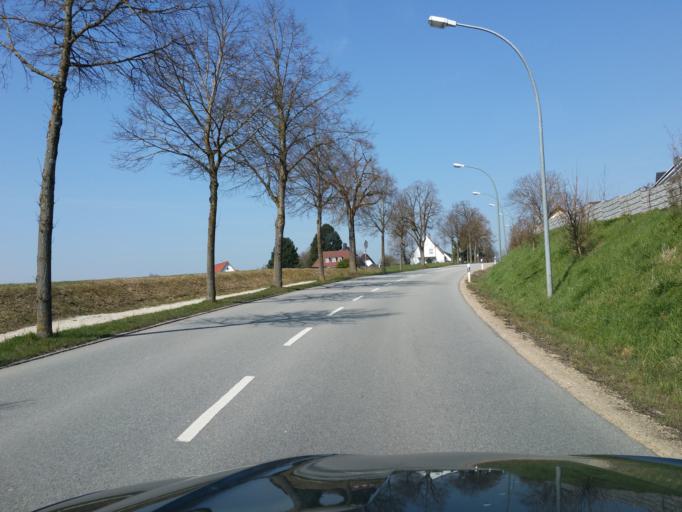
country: DE
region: Bavaria
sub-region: Lower Bavaria
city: Landshut
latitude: 48.5237
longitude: 12.1697
